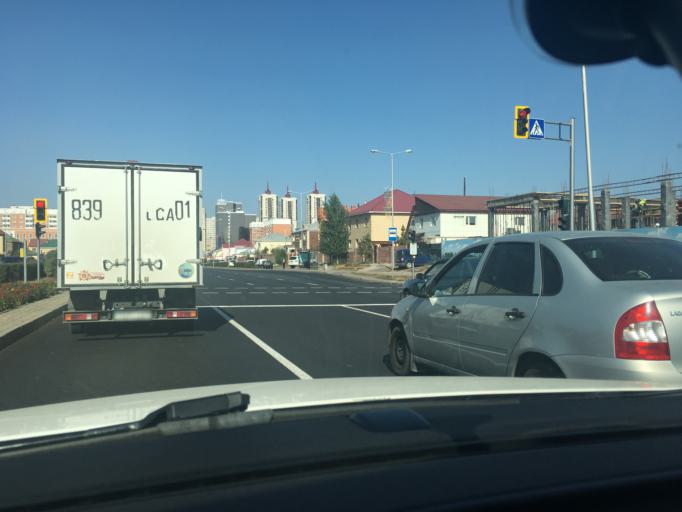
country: KZ
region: Astana Qalasy
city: Astana
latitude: 51.1315
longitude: 71.4707
